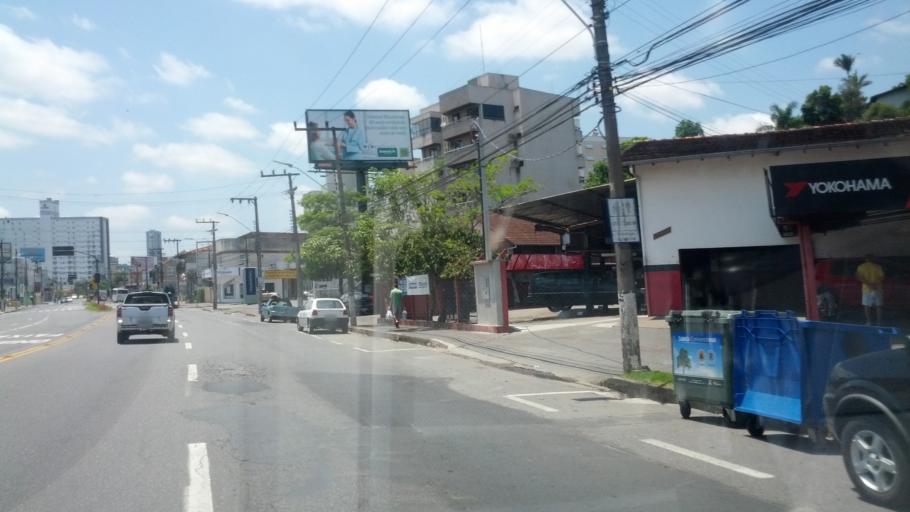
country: BR
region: Santa Catarina
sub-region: Blumenau
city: Blumenau
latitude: -26.9132
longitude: -49.0787
